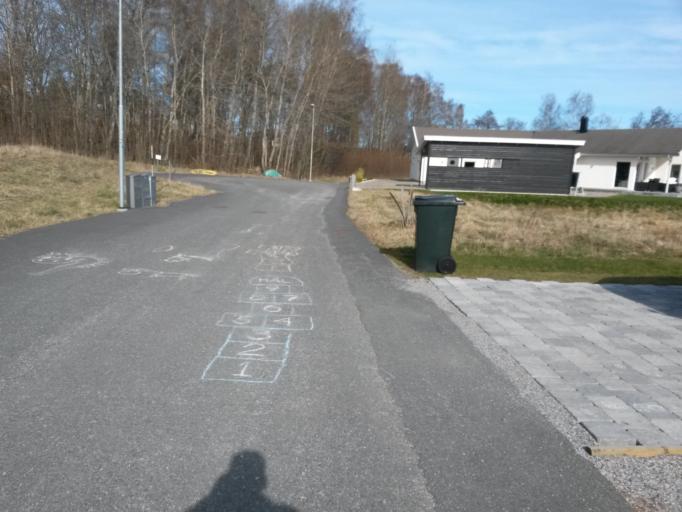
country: SE
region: Vaestra Goetaland
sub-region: Vargarda Kommun
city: Vargarda
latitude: 58.0247
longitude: 12.8059
